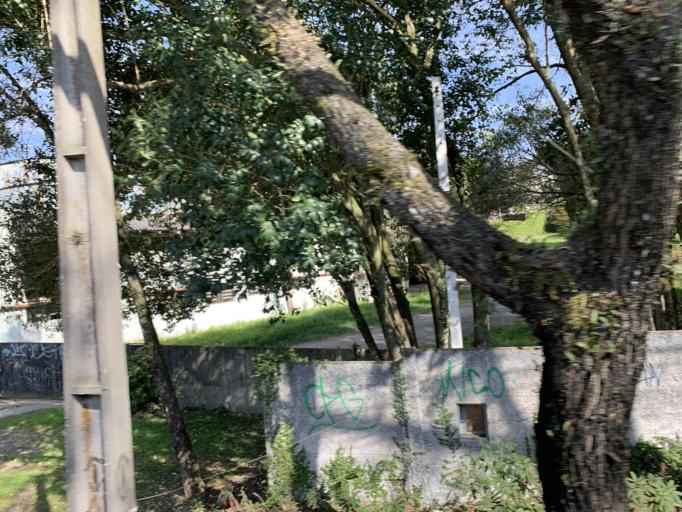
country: BR
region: Parana
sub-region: Curitiba
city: Curitiba
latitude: -25.4030
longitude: -49.3259
